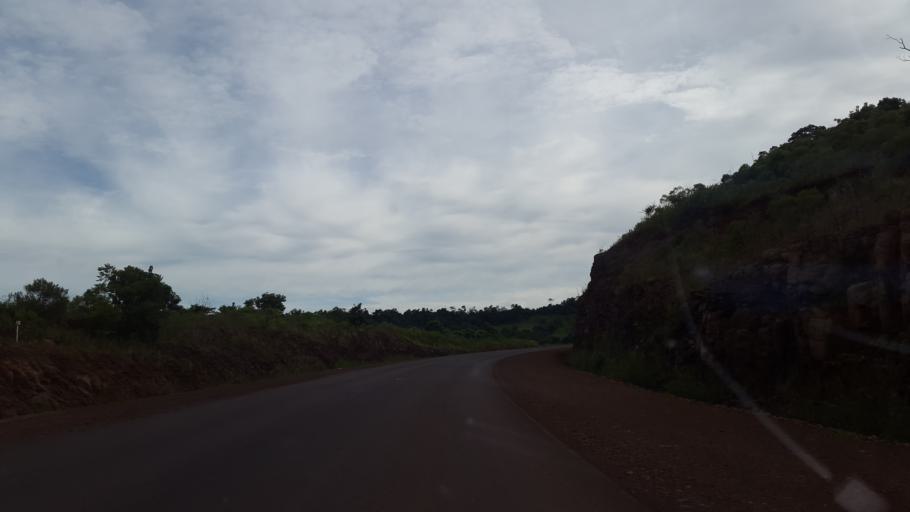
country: AR
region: Misiones
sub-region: Departamento de San Pedro
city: San Pedro
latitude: -26.4573
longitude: -53.8719
